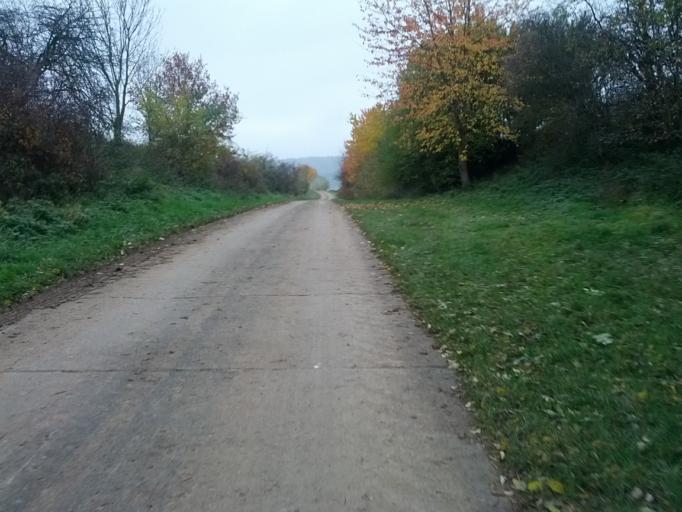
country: DE
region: Thuringia
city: Seebach
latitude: 50.9871
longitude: 10.4067
